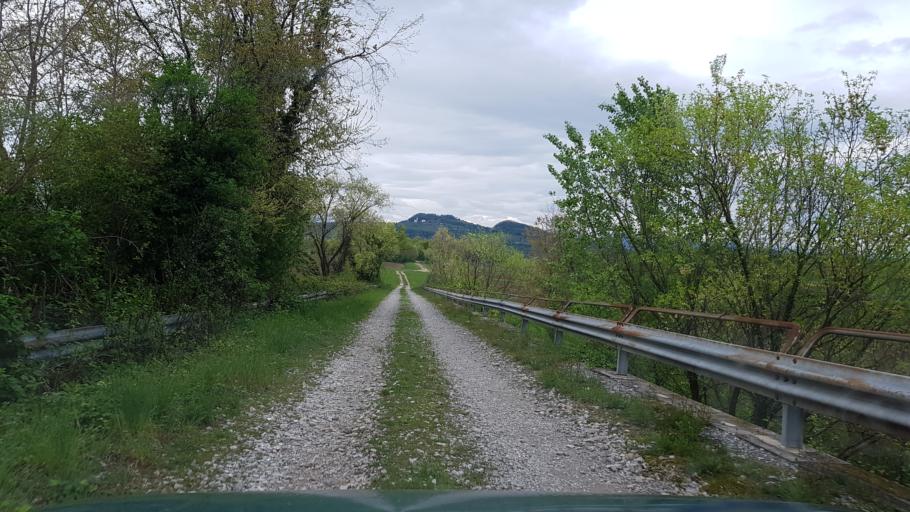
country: IT
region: Friuli Venezia Giulia
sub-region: Provincia di Gorizia
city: Mariano del Friuli
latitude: 45.9305
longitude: 13.4701
